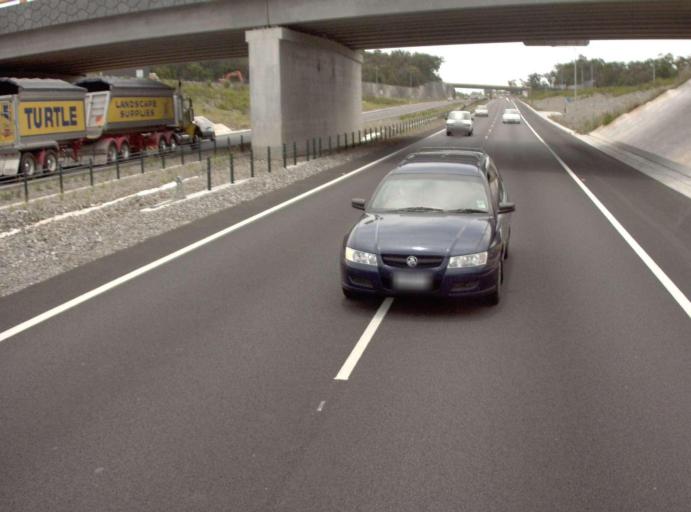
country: AU
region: Victoria
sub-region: Frankston
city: Langwarrin
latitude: -38.1819
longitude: 145.1592
